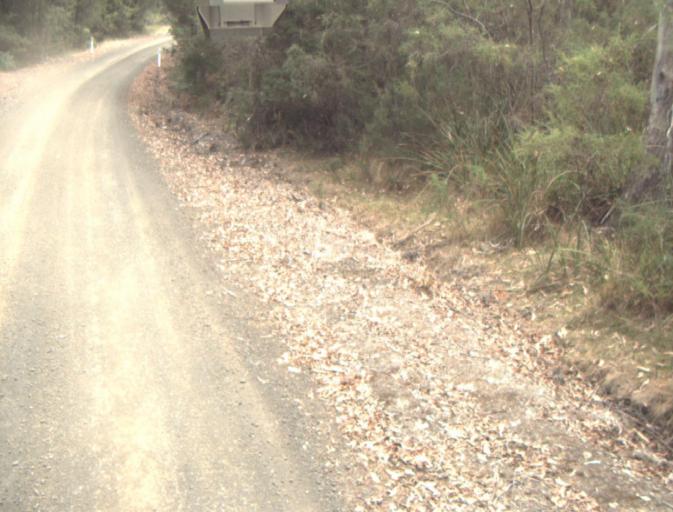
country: AU
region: Tasmania
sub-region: Launceston
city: Mayfield
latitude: -41.2739
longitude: 147.0515
